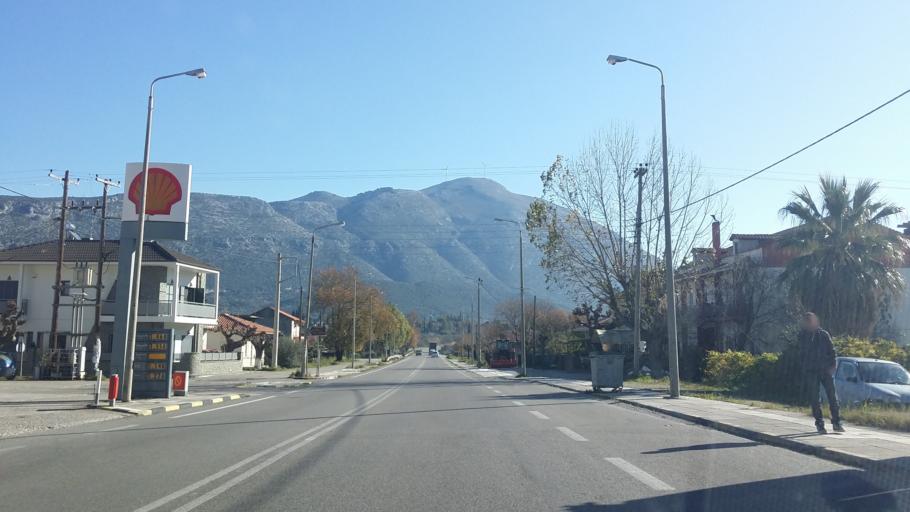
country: GR
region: West Greece
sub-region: Nomos Aitolias kai Akarnanias
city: Galatas
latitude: 38.3759
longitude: 21.6290
